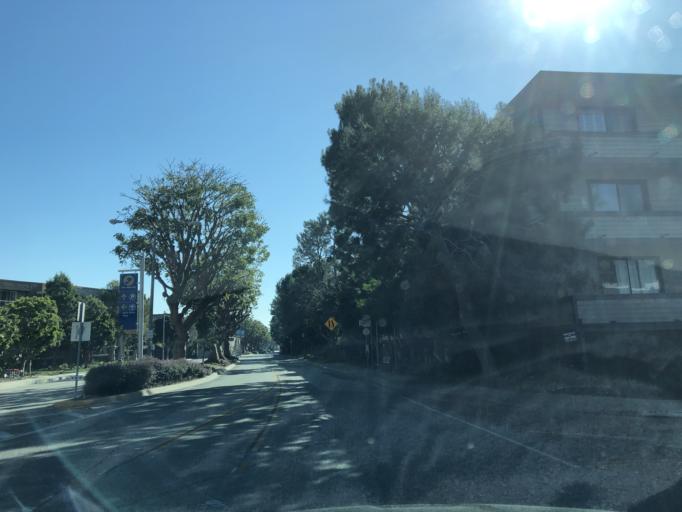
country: US
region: California
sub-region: Los Angeles County
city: Marina del Rey
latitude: 33.9714
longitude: -118.4558
